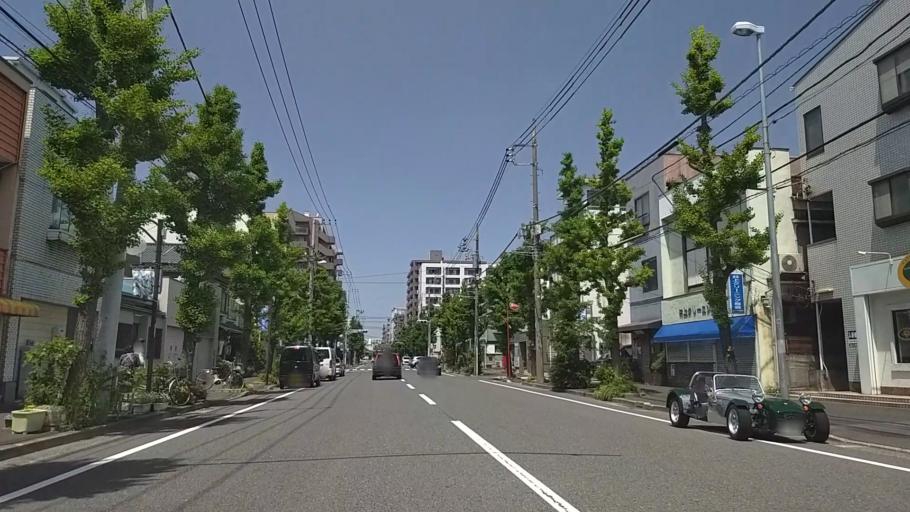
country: JP
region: Kanagawa
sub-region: Kawasaki-shi
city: Kawasaki
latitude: 35.5170
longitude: 139.7141
